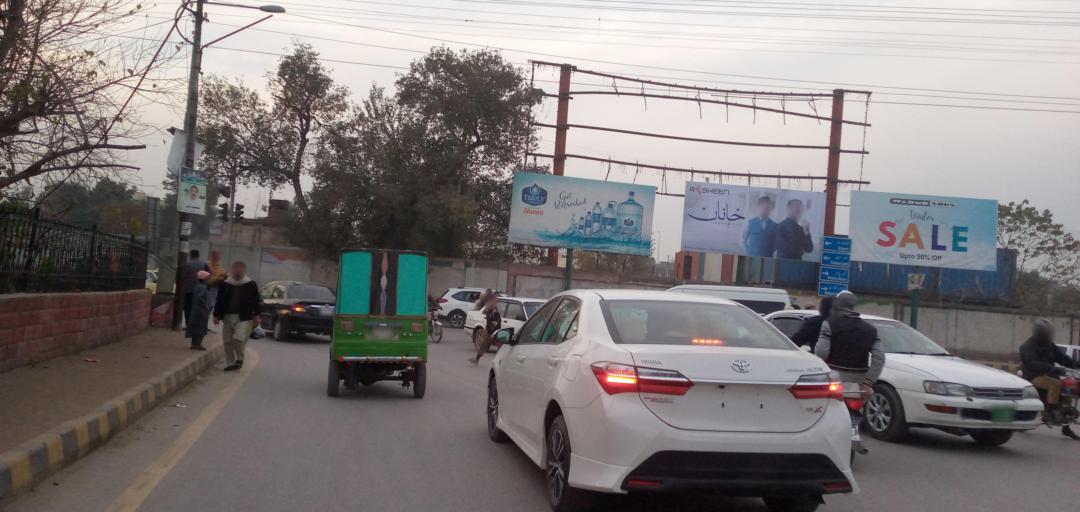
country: PK
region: Khyber Pakhtunkhwa
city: Peshawar
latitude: 34.0011
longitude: 71.5518
